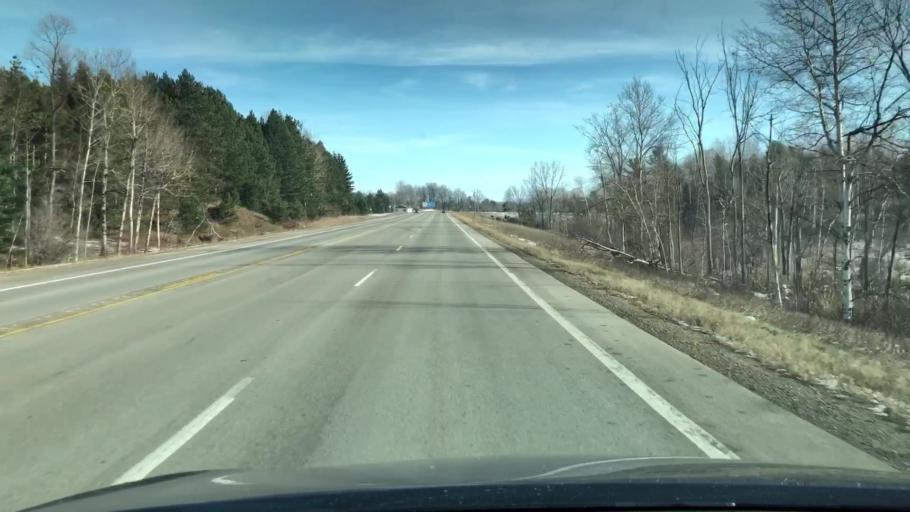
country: US
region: Michigan
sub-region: Kalkaska County
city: Rapid City
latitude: 44.7775
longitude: -85.3567
